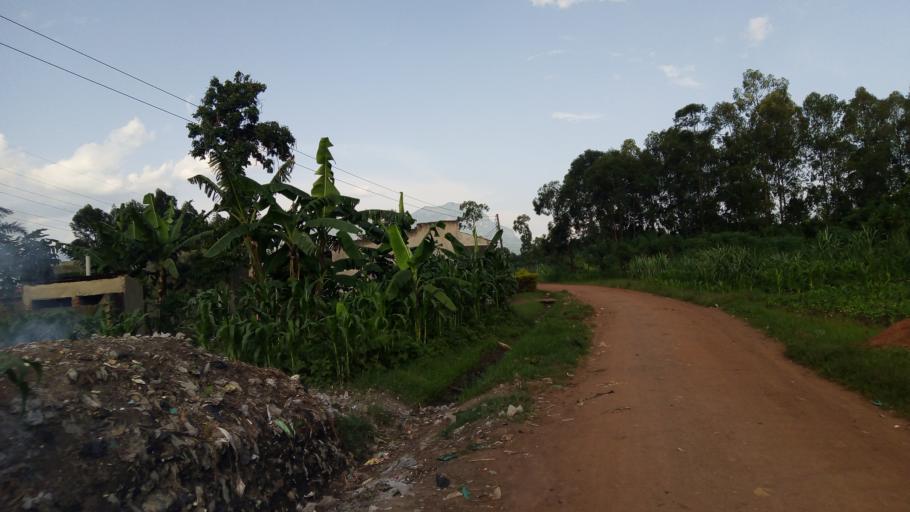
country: UG
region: Eastern Region
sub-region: Mbale District
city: Mbale
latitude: 1.0557
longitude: 34.1619
